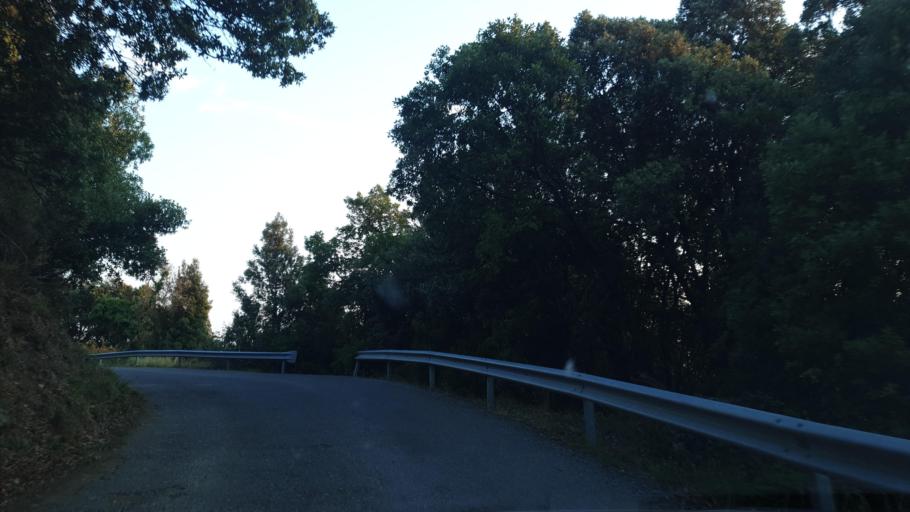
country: IT
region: Liguria
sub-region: Provincia di La Spezia
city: Bonassola
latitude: 44.1940
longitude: 9.5873
